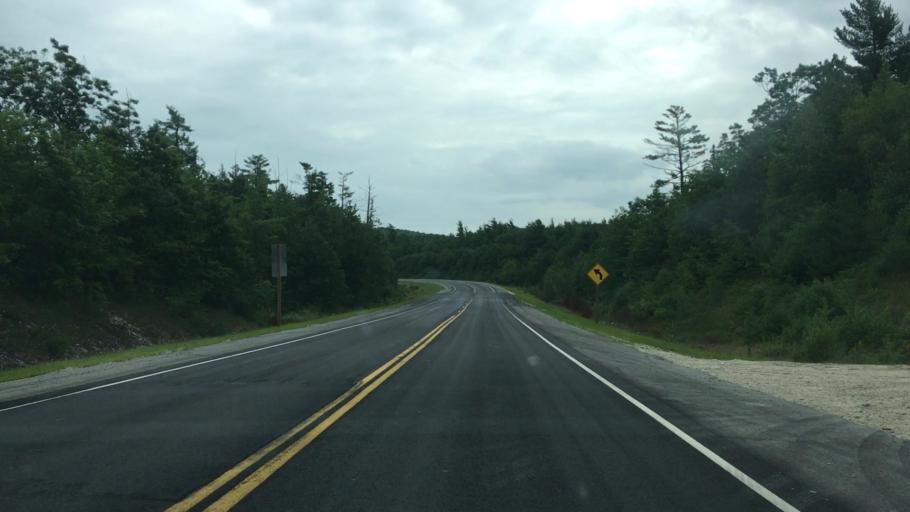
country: US
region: Maine
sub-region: Washington County
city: Cherryfield
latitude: 44.8793
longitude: -67.8664
